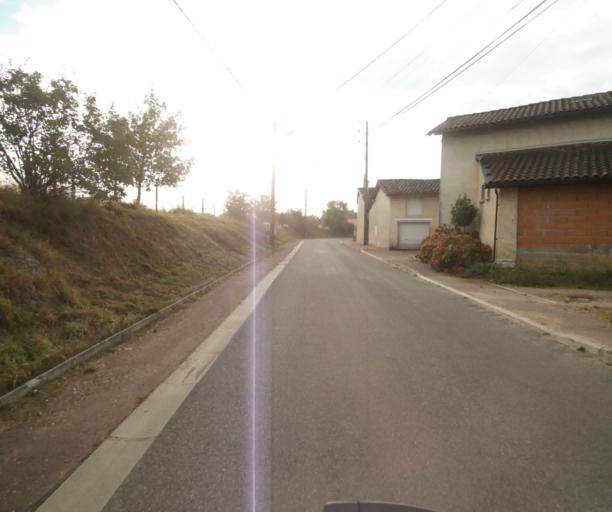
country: FR
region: Midi-Pyrenees
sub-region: Departement du Tarn-et-Garonne
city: Montech
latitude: 43.9628
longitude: 1.2273
